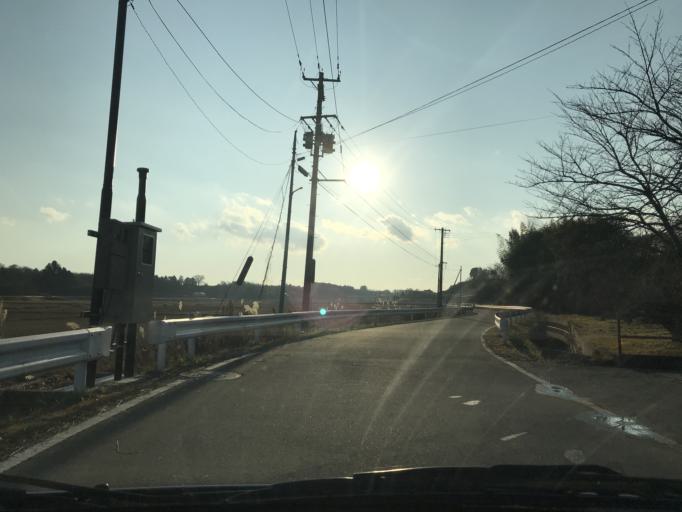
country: JP
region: Miyagi
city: Wakuya
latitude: 38.7074
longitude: 141.1275
